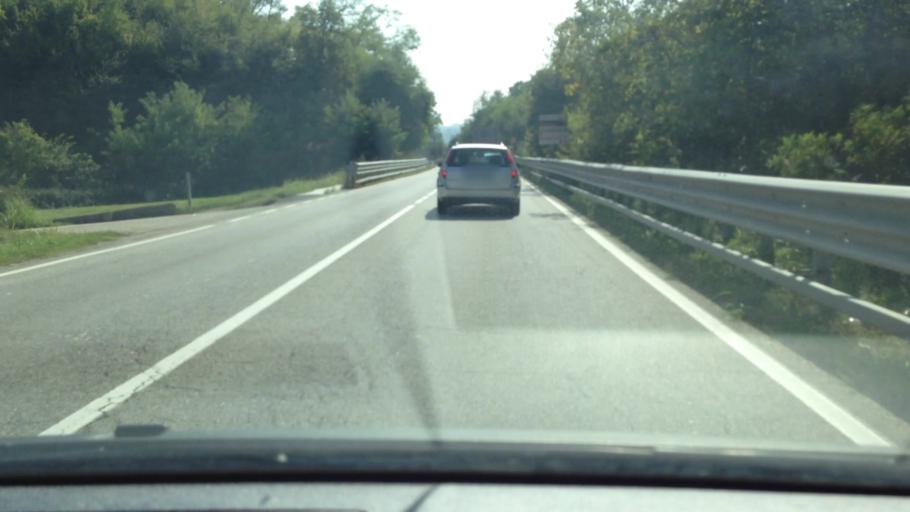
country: IT
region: Piedmont
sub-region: Provincia di Asti
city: Castello di Annone
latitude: 44.8857
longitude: 8.3102
